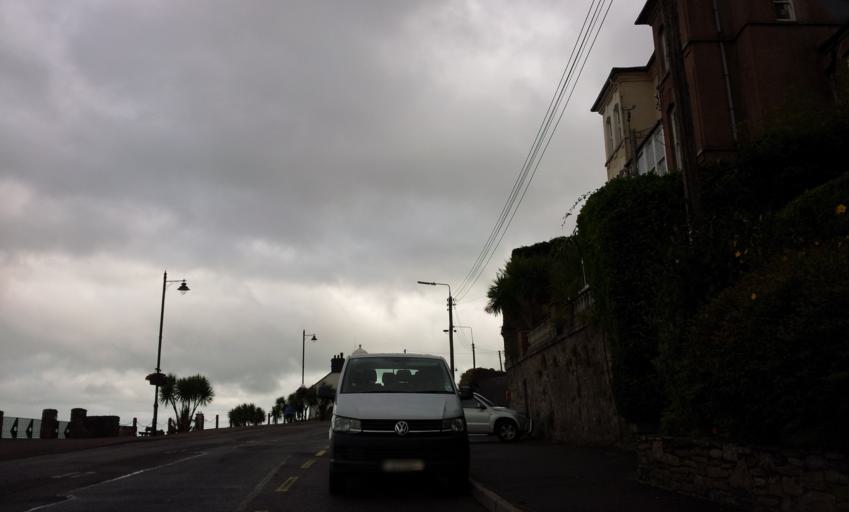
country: IE
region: Munster
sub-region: County Cork
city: Youghal
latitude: 51.9440
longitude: -7.8426
